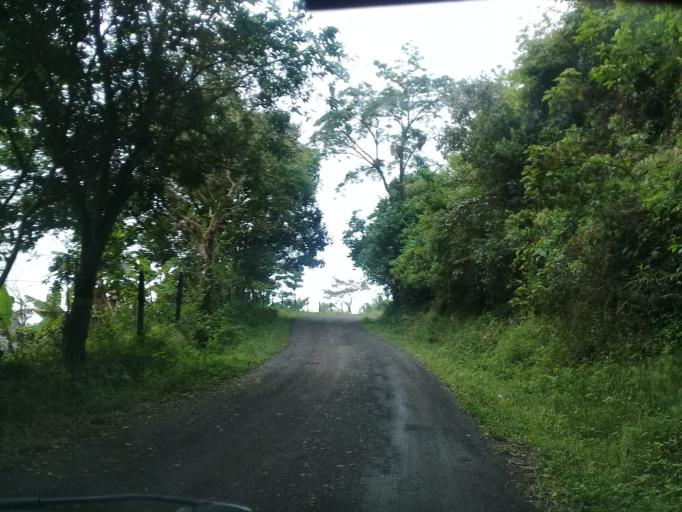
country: CO
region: Cundinamarca
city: Quipile
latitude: 4.7227
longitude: -74.5554
